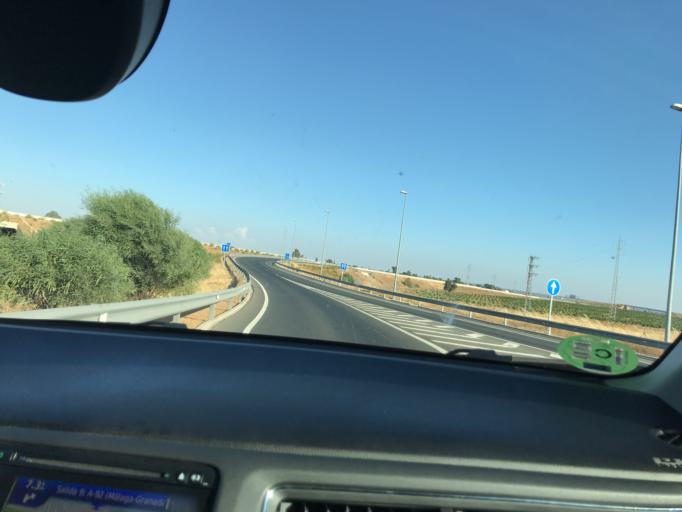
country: ES
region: Andalusia
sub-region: Provincia de Sevilla
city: Alcala de Guadaira
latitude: 37.4305
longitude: -5.8454
